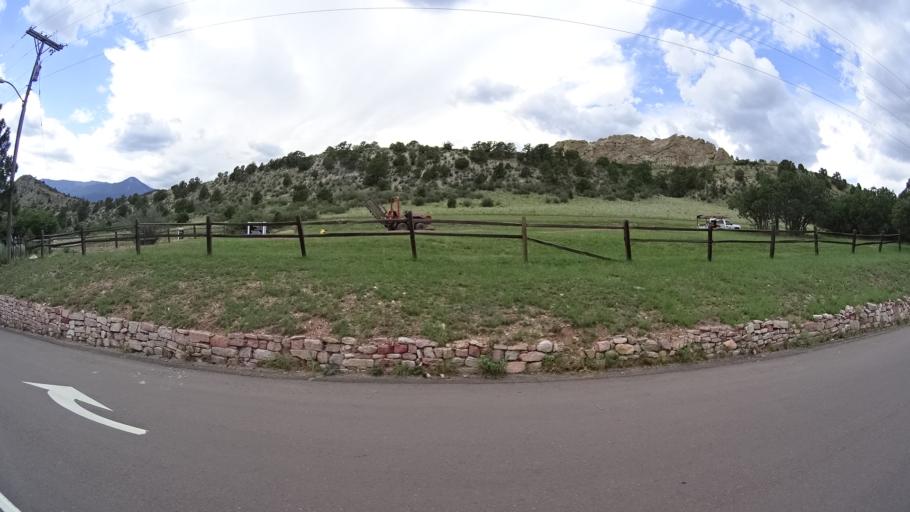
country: US
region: Colorado
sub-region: El Paso County
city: Manitou Springs
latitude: 38.8920
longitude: -104.8750
